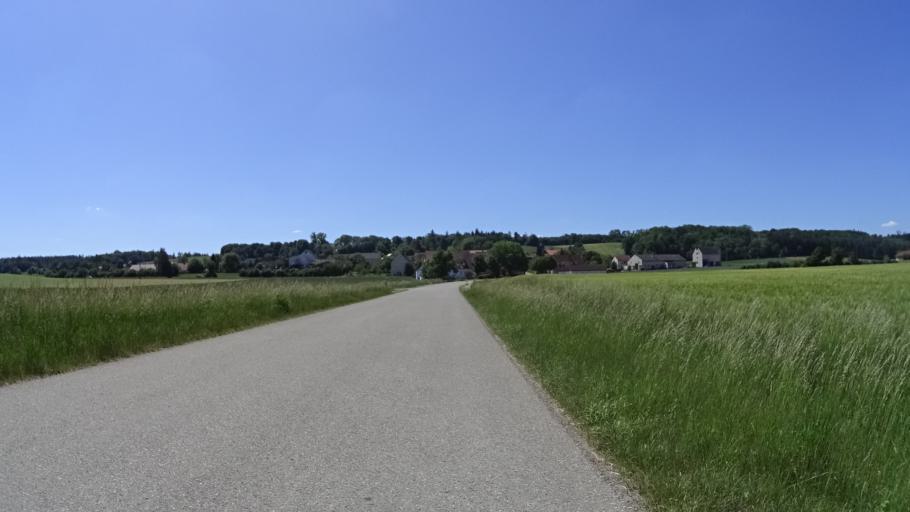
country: DE
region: Bavaria
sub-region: Regierungsbezirk Mittelfranken
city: Absberg
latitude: 49.1129
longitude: 10.8884
